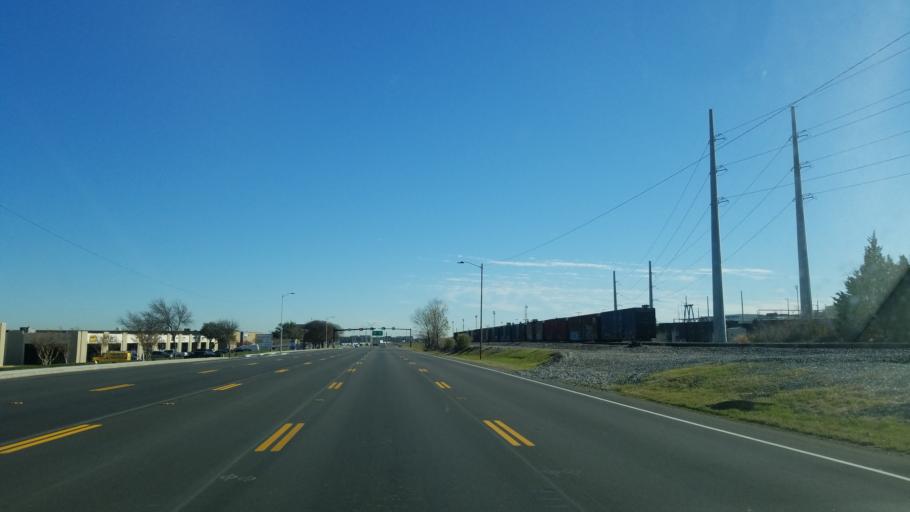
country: US
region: Texas
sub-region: Tarrant County
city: Arlington
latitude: 32.7431
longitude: -97.0723
